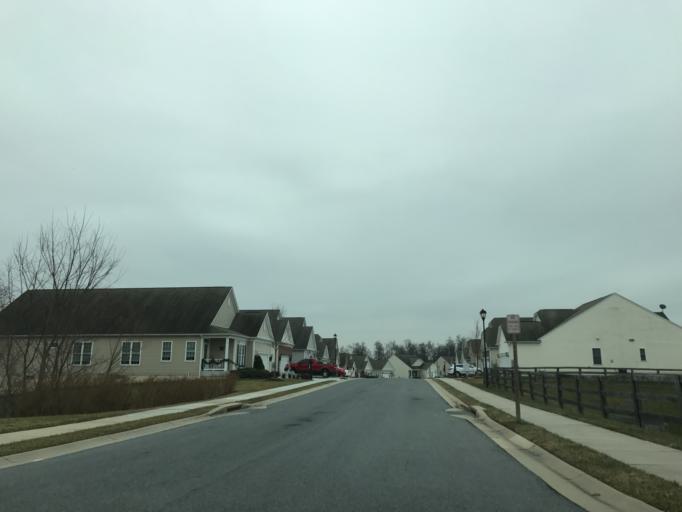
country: US
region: Maryland
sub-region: Carroll County
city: Taneytown
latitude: 39.6429
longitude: -77.1525
